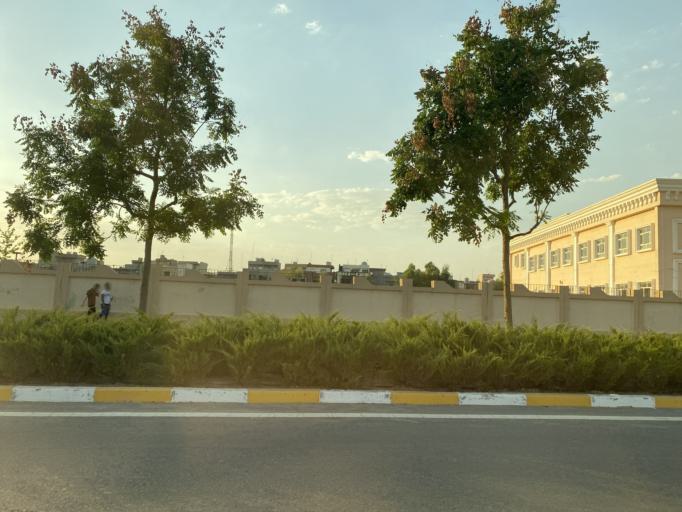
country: IQ
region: Arbil
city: Erbil
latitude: 36.2194
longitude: 44.0026
